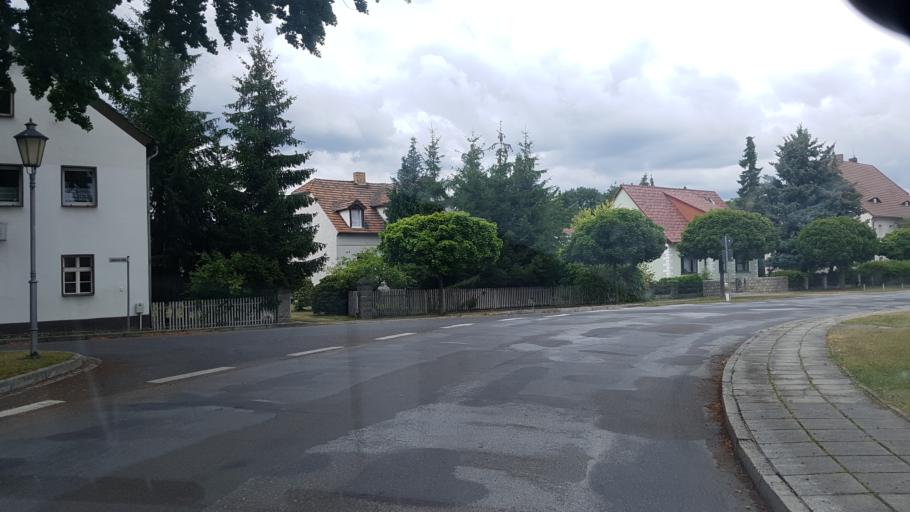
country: DE
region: Saxony
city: Klitten
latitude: 51.3809
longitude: 14.6625
